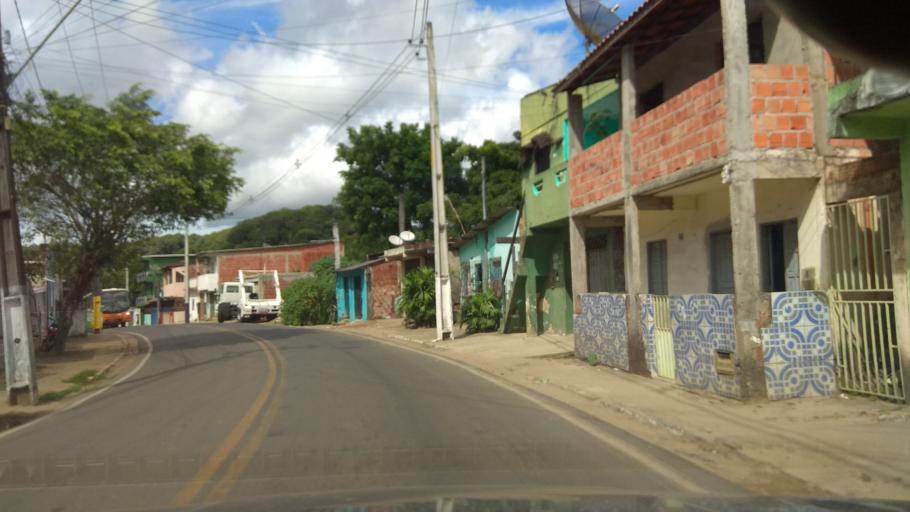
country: BR
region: Bahia
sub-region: Ilheus
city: Ilheus
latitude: -14.7867
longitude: -39.0606
